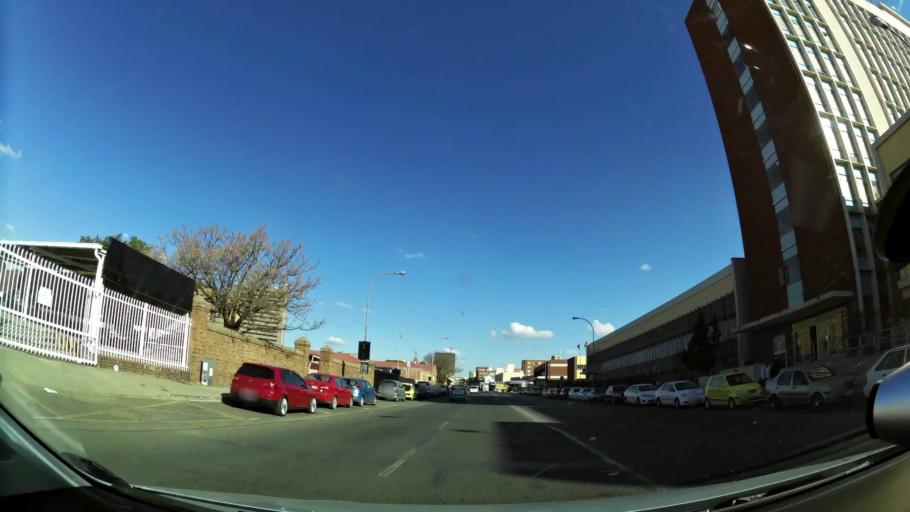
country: ZA
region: Northern Cape
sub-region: Frances Baard District Municipality
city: Kimberley
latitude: -28.7346
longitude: 24.7637
